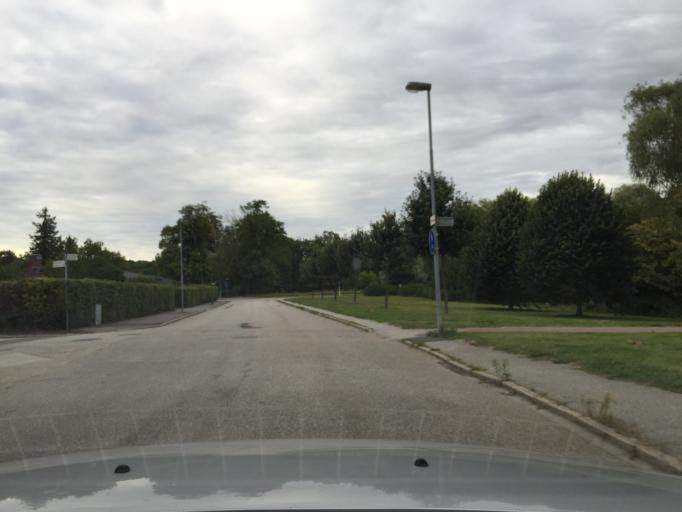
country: SE
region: Skane
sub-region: Burlovs Kommun
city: Arloev
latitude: 55.5989
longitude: 13.0785
